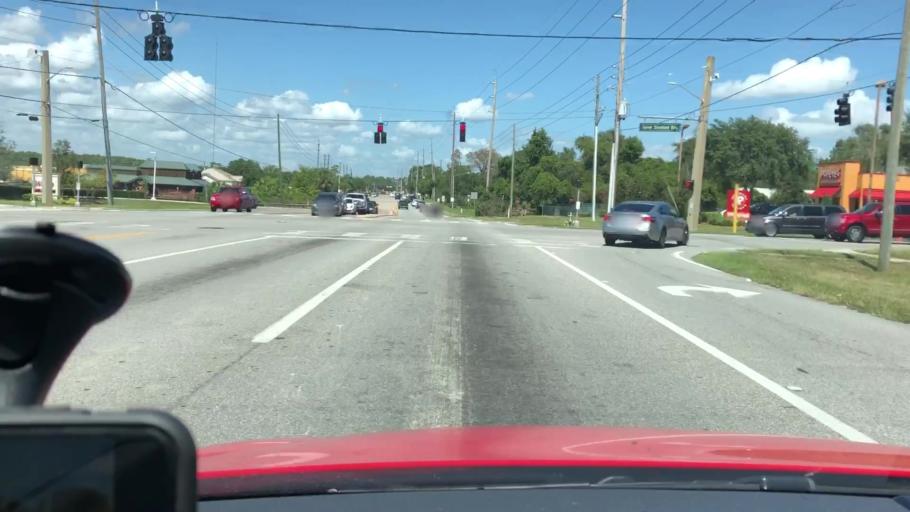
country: US
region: Florida
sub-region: Volusia County
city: Orange City
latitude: 28.9167
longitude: -81.2947
